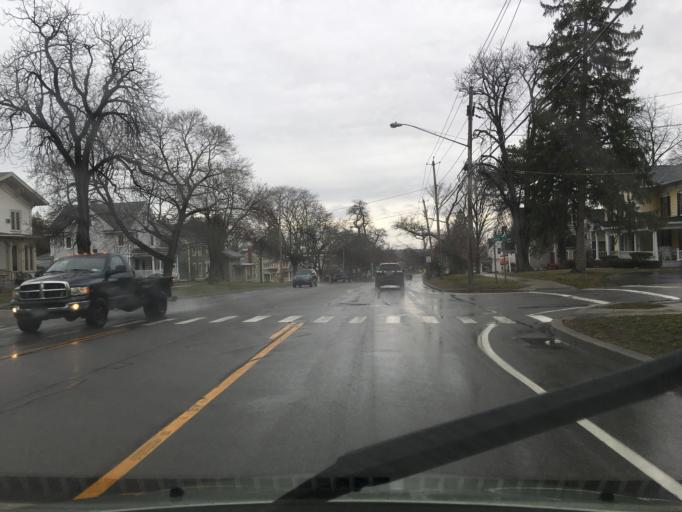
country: US
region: New York
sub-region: Livingston County
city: Avon
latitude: 42.9111
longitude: -77.7407
